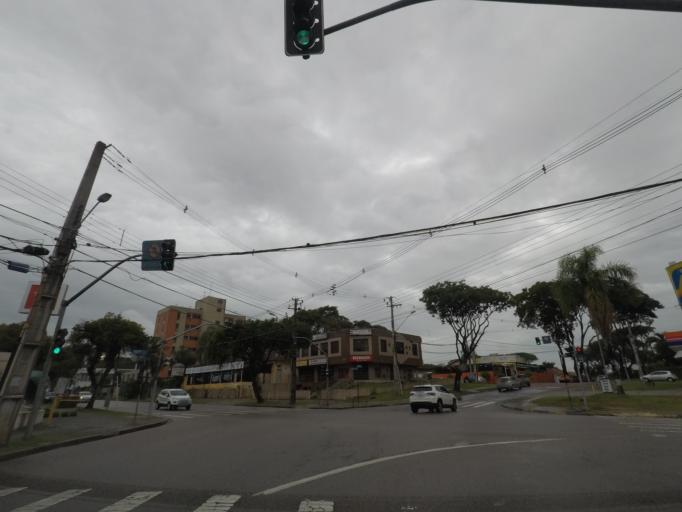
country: BR
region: Parana
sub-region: Curitiba
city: Curitiba
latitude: -25.4529
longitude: -49.2780
